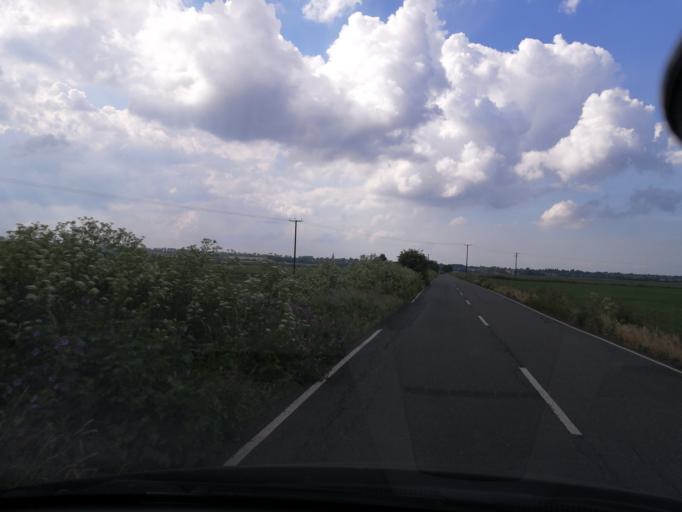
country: GB
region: England
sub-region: Cambridgeshire
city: Yaxley
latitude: 52.4953
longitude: -0.2453
